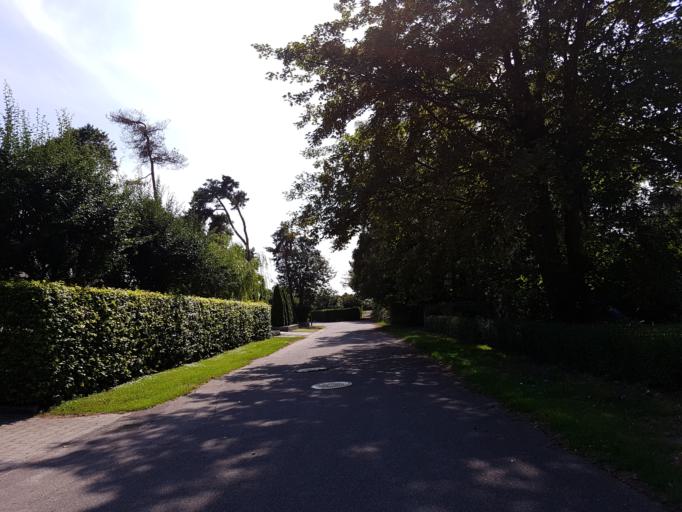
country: DK
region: Zealand
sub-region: Guldborgsund Kommune
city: Nykobing Falster
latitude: 54.5715
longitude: 11.9384
